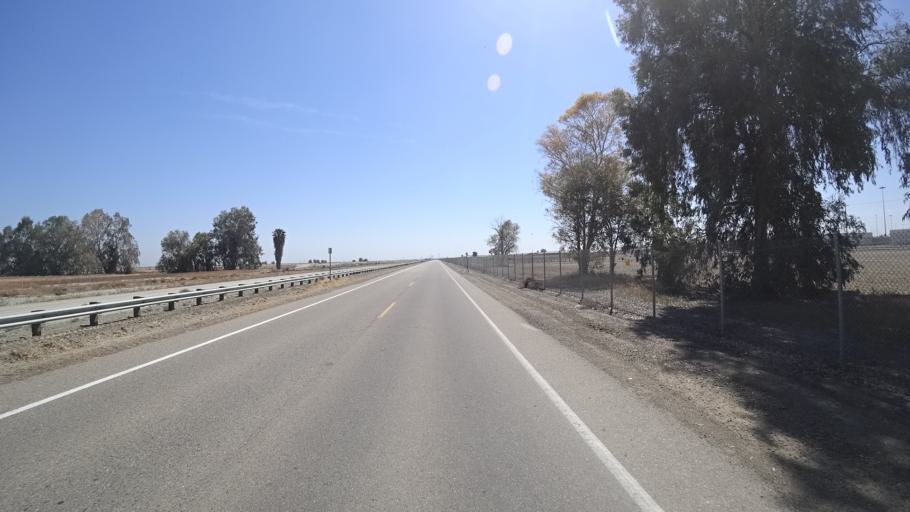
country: US
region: California
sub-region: Kings County
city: Corcoran
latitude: 36.0650
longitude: -119.5487
